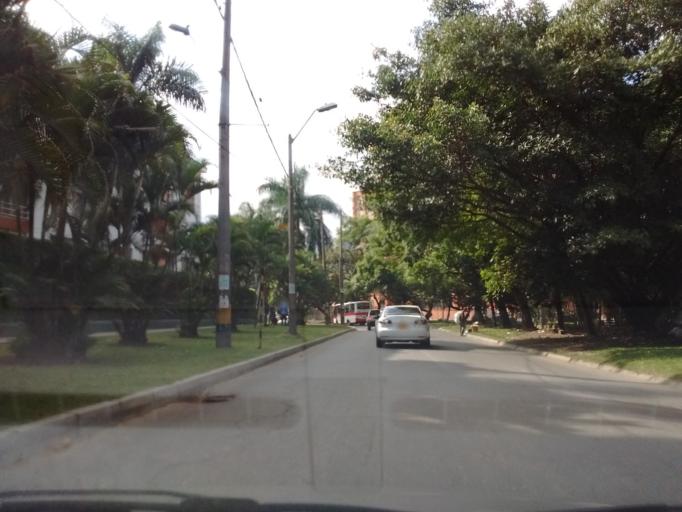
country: CO
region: Antioquia
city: Itagui
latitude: 6.2299
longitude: -75.6049
